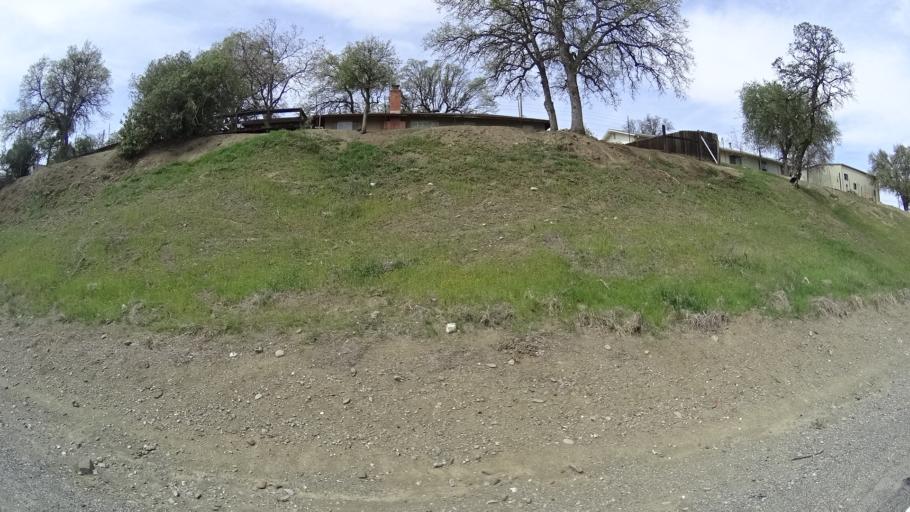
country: US
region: California
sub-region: Glenn County
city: Willows
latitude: 39.6050
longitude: -122.5369
